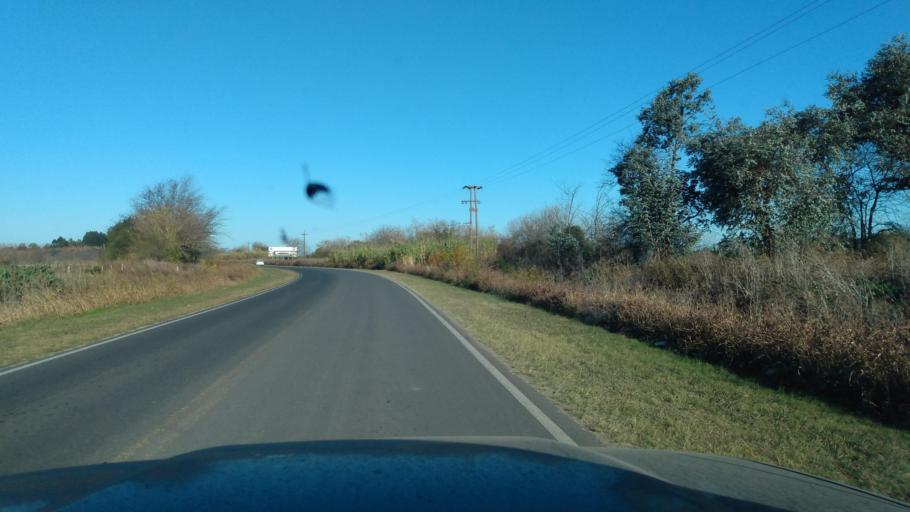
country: AR
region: Buenos Aires
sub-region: Partido de Lujan
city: Lujan
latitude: -34.4938
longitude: -59.2089
